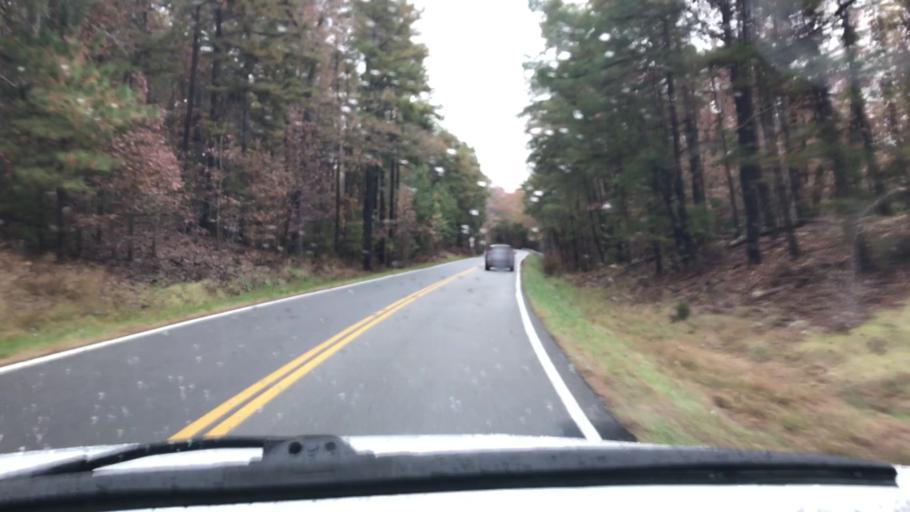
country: US
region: Virginia
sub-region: Henrico County
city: Short Pump
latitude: 37.6100
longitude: -77.6989
